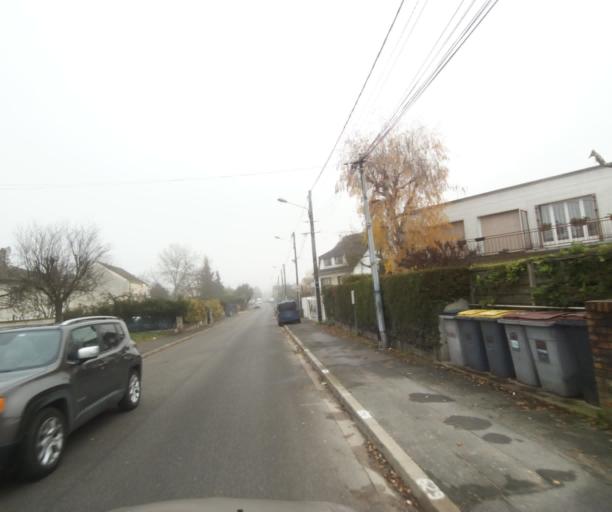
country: FR
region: Ile-de-France
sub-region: Departement de Seine-Saint-Denis
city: Coubron
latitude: 48.9126
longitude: 2.5873
